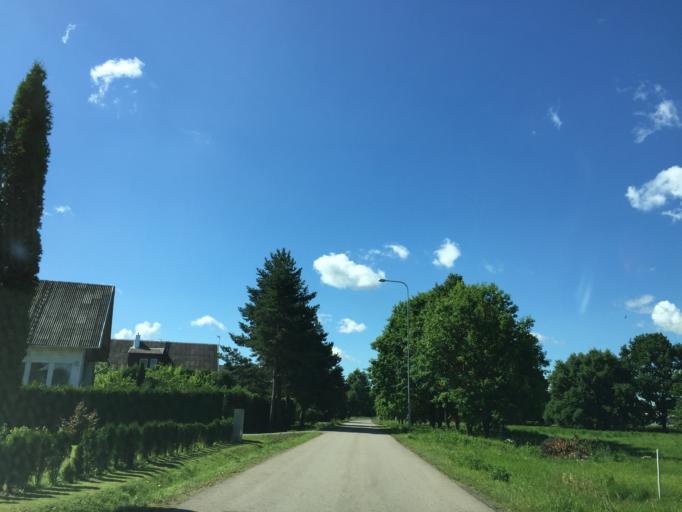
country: LT
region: Panevezys
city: Pasvalys
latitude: 56.0719
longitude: 24.4418
